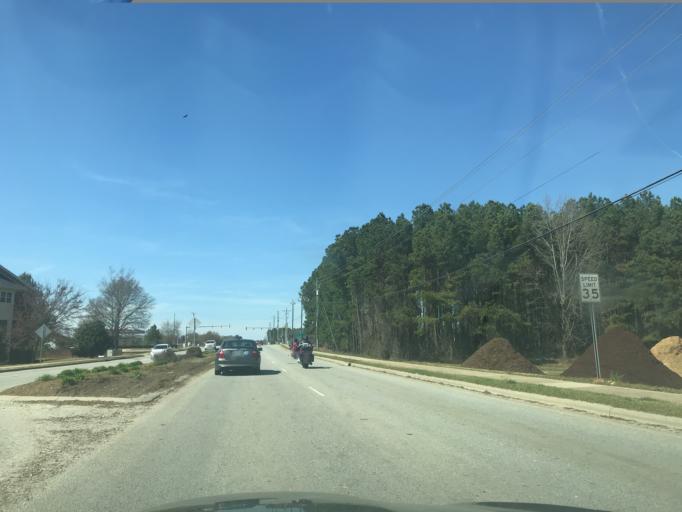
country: US
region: North Carolina
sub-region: Wake County
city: Fuquay-Varina
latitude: 35.6005
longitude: -78.8020
